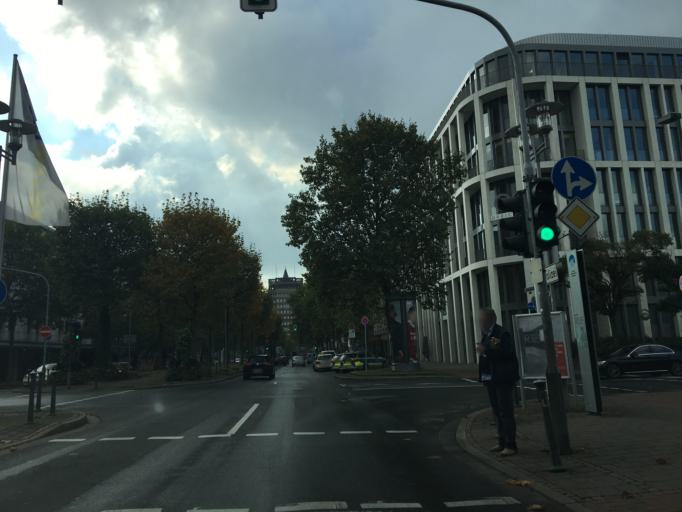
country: DE
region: North Rhine-Westphalia
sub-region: Regierungsbezirk Dusseldorf
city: Dusseldorf
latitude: 51.2281
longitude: 6.7768
